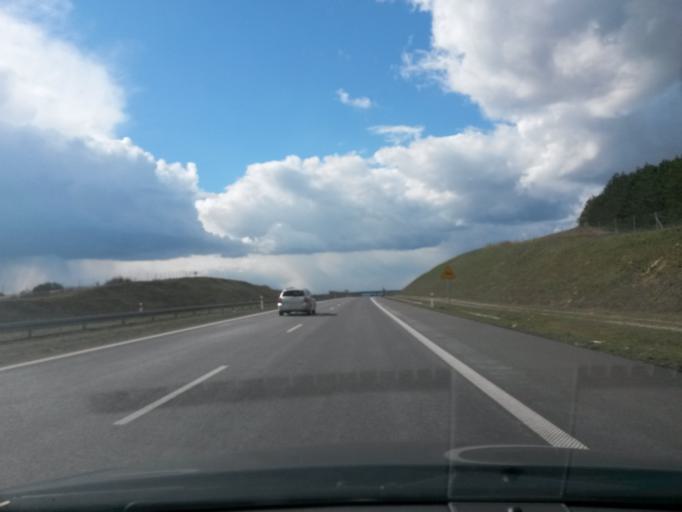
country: PL
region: Greater Poland Voivodeship
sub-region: Powiat kolski
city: Koscielec
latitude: 52.1432
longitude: 18.5240
